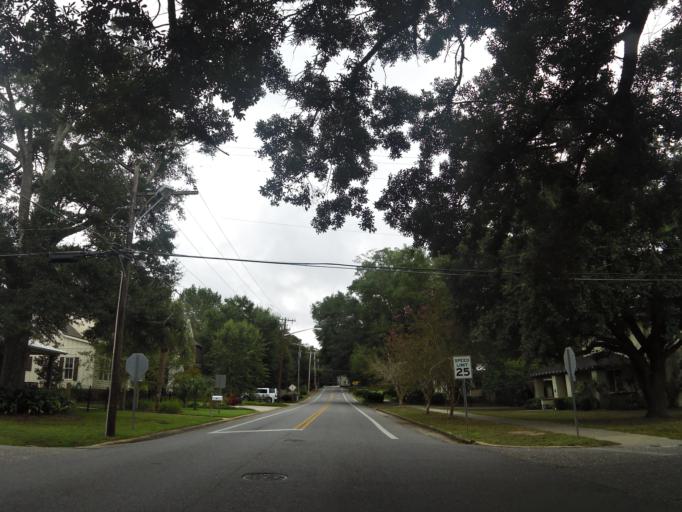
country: US
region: Alabama
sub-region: Baldwin County
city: Fairhope
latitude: 30.5201
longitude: -87.9100
